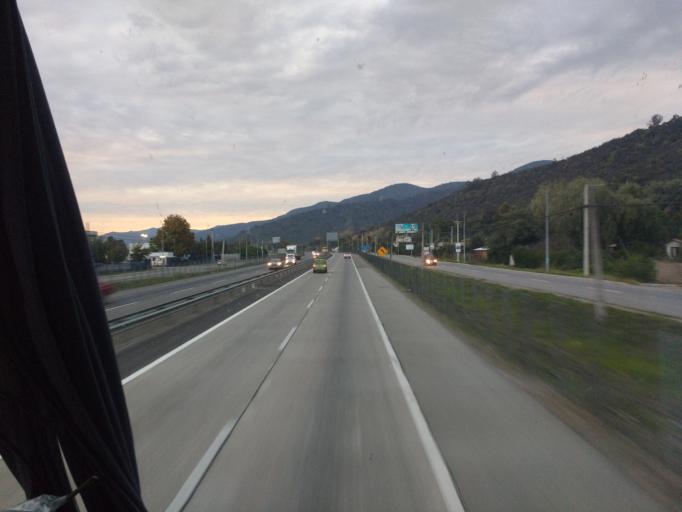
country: CL
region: Santiago Metropolitan
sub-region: Provincia de Chacabuco
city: Lampa
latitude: -33.4131
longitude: -71.0553
